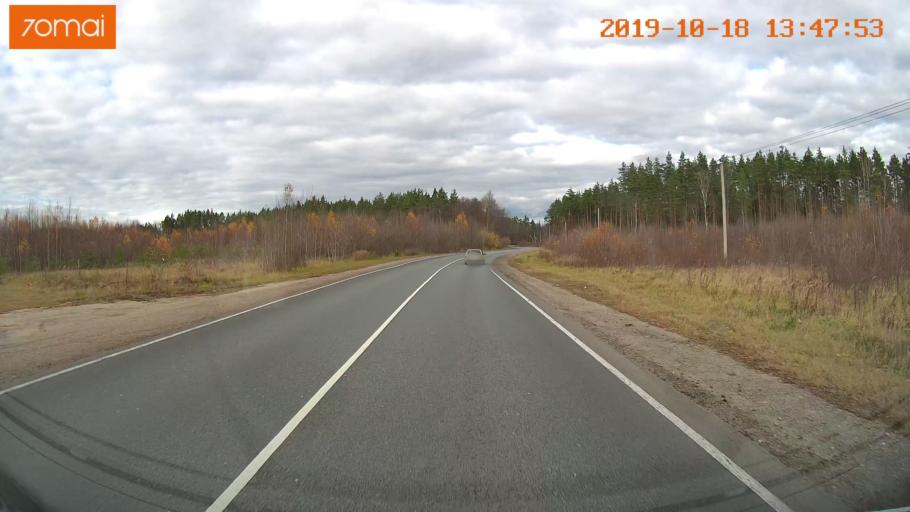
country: RU
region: Moskovskaya
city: Radovitskiy
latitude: 54.9817
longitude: 39.9515
